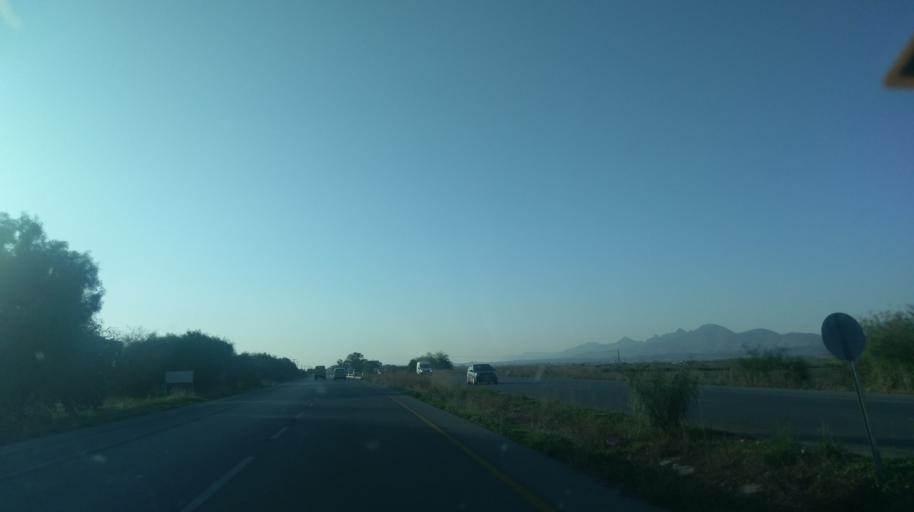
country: CY
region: Larnaka
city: Athienou
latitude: 35.2106
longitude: 33.5611
